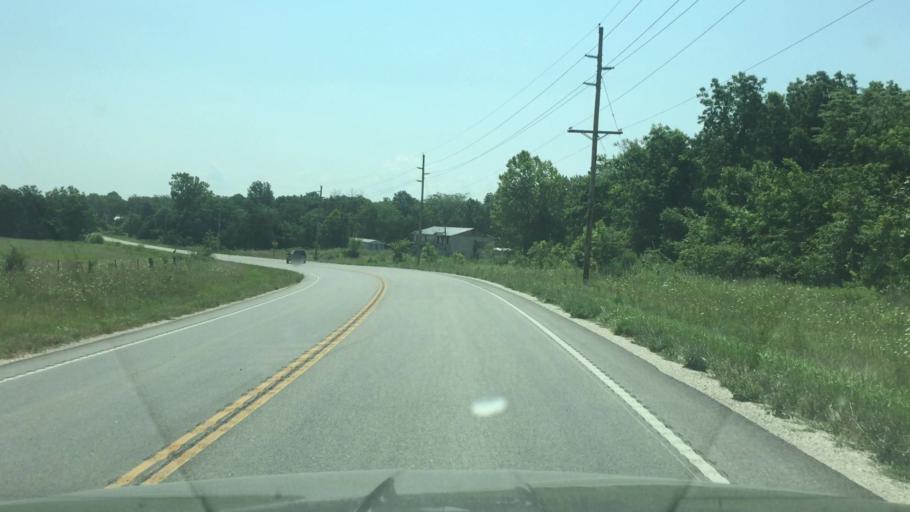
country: US
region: Missouri
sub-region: Miller County
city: Eldon
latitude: 38.3817
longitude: -92.6816
